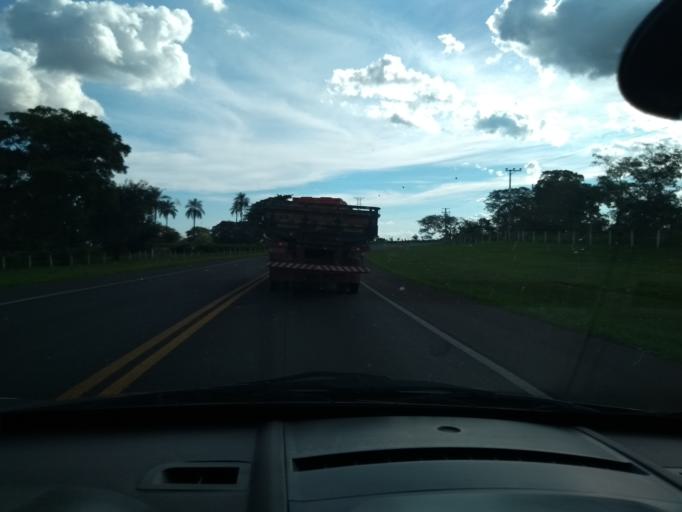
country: BR
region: Sao Paulo
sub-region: Casa Branca
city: Casa Branca
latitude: -21.7972
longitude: -47.0758
